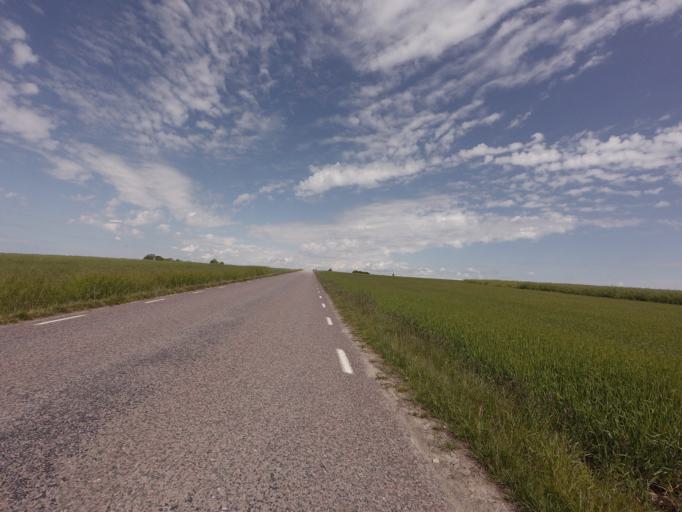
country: SE
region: Skane
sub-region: Trelleborgs Kommun
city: Skare
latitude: 55.4390
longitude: 13.0731
